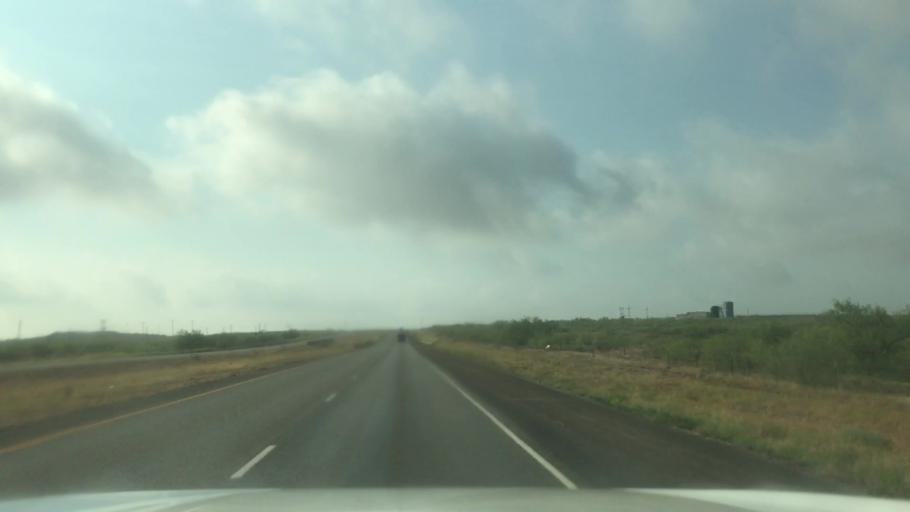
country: US
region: Texas
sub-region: Garza County
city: Post
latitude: 33.1678
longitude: -101.3527
